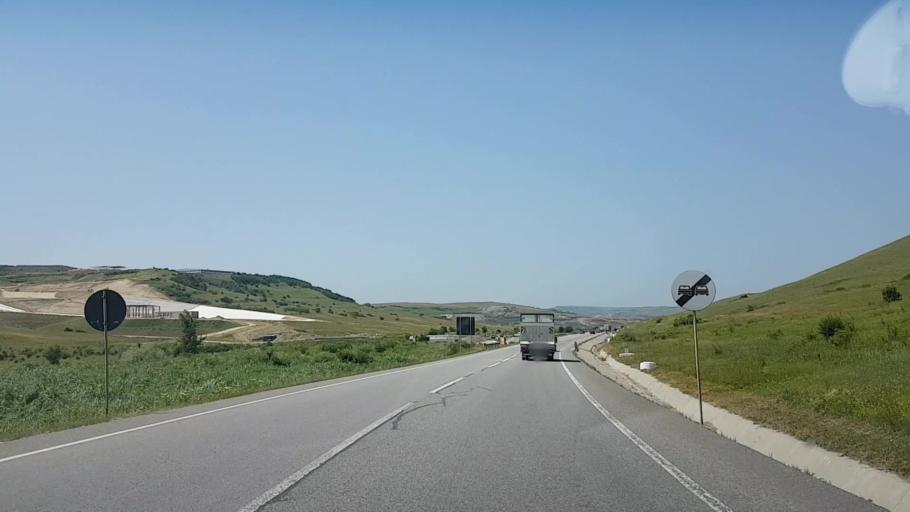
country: RO
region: Cluj
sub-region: Comuna Apahida
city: Dezmir
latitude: 46.7478
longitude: 23.7083
